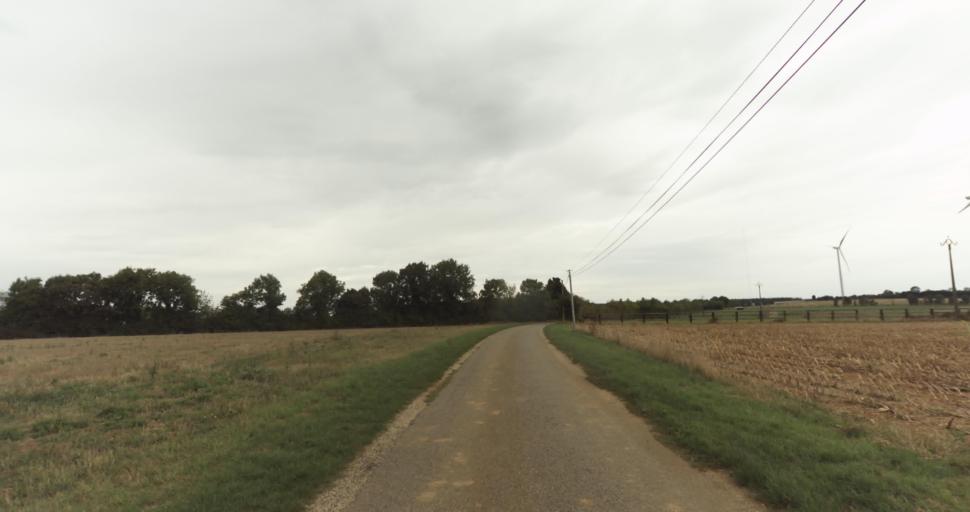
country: FR
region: Lower Normandy
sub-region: Departement de l'Orne
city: Sainte-Gauburge-Sainte-Colombe
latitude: 48.7328
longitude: 0.3652
